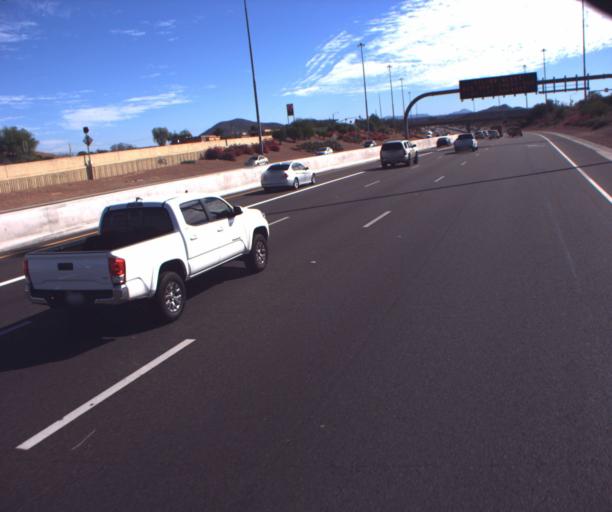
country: US
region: Arizona
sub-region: Maricopa County
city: Glendale
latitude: 33.6688
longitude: -112.0866
